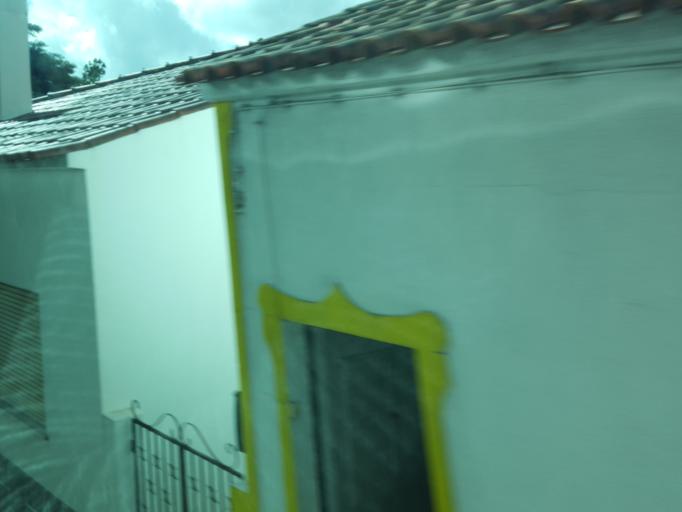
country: PT
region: Faro
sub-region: Monchique
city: Monchique
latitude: 37.3034
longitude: -8.5620
